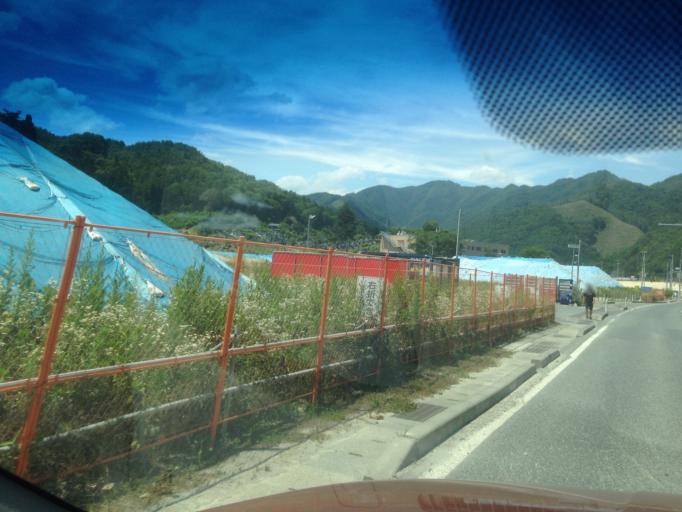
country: JP
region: Iwate
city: Otsuchi
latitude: 39.3289
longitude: 141.8850
